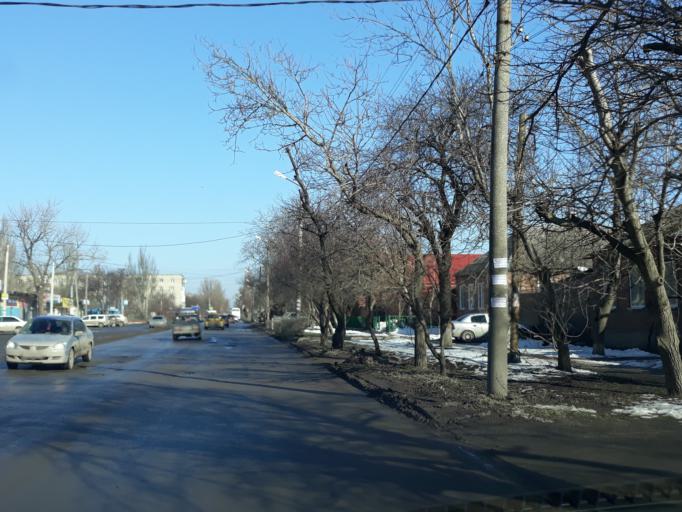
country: RU
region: Rostov
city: Taganrog
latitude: 47.2306
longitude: 38.8764
